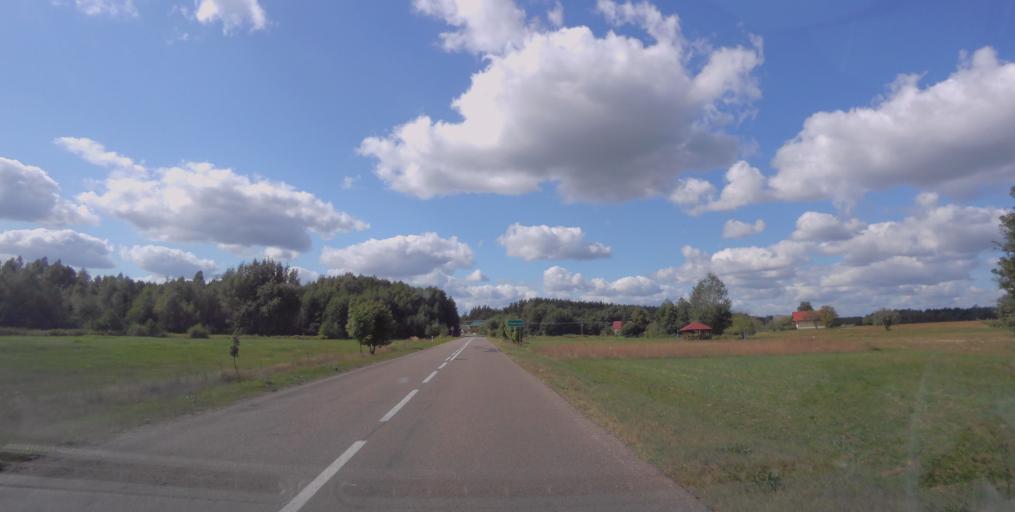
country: PL
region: Subcarpathian Voivodeship
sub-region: Powiat stalowowolski
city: Bojanow
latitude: 50.3961
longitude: 22.0088
